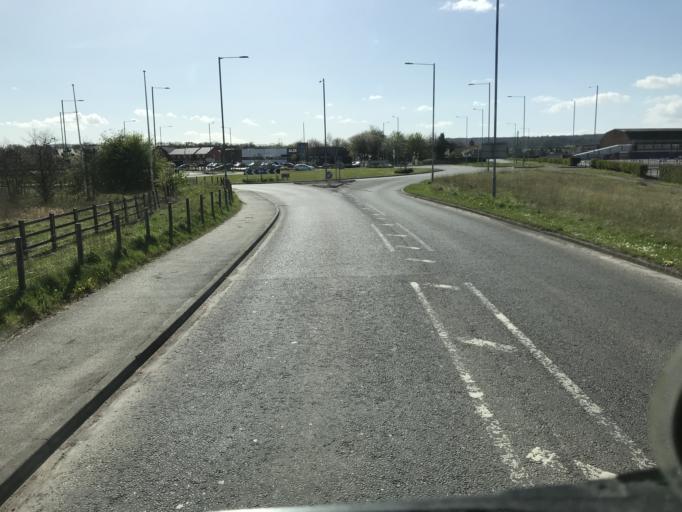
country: GB
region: Wales
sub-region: County of Flintshire
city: Hawarden
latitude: 53.1709
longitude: -2.9754
